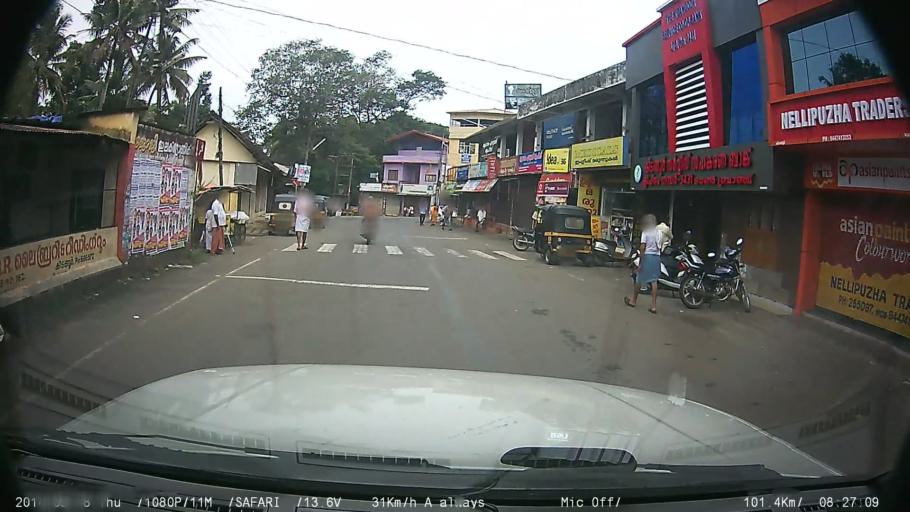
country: IN
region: Kerala
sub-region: Kottayam
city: Palackattumala
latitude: 9.6842
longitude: 76.6104
